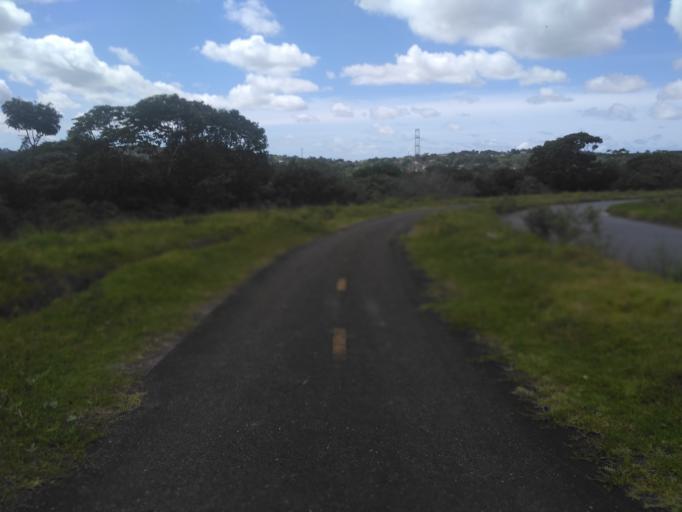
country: BR
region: Pernambuco
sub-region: Sao Lourenco Da Mata
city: Sao Lourenco da Mata
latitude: -8.0397
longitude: -35.0000
